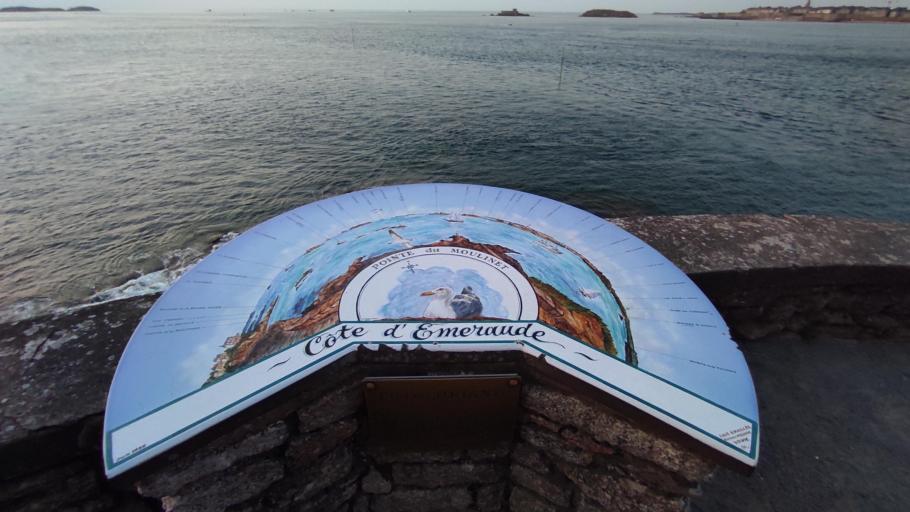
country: FR
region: Brittany
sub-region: Departement d'Ille-et-Vilaine
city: Dinard
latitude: 48.6390
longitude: -2.0478
